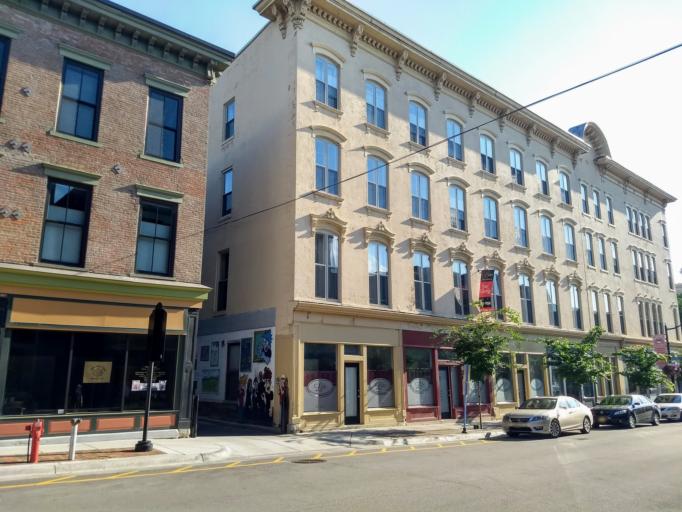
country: US
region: Indiana
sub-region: Tippecanoe County
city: Lafayette
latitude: 40.4192
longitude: -86.8911
